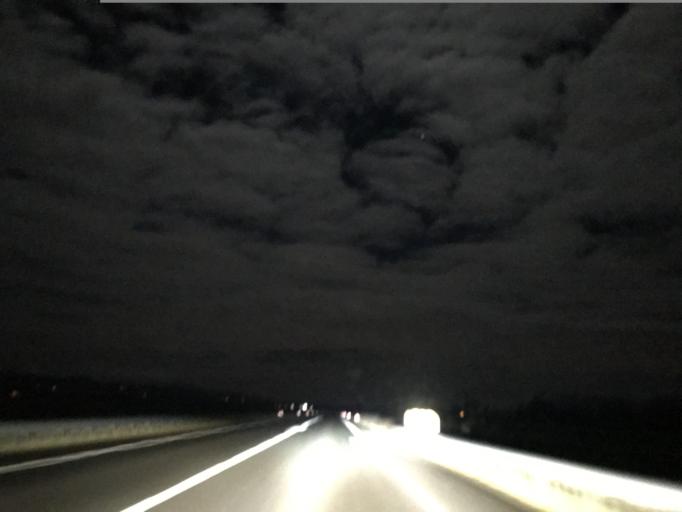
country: FR
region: Auvergne
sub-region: Departement de l'Allier
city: Saint-Yorre
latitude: 46.0649
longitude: 3.4457
